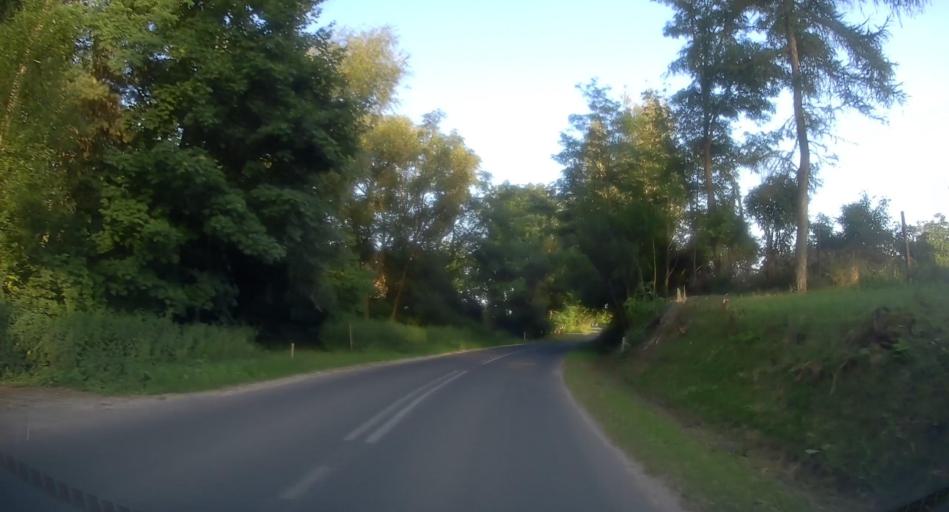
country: PL
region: Lodz Voivodeship
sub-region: Powiat skierniewicki
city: Kowiesy
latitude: 51.8965
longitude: 20.3791
